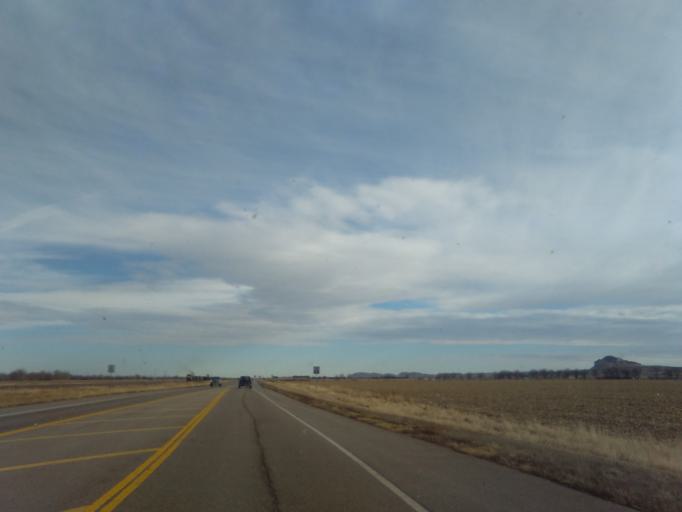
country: US
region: Nebraska
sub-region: Scotts Bluff County
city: Gering
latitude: 41.7826
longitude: -103.5142
